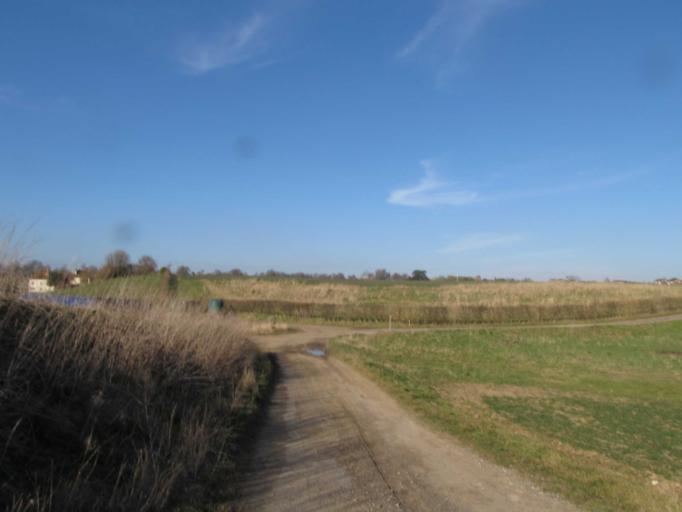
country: GB
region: England
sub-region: West Sussex
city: Petworth
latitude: 50.9791
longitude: -0.6193
